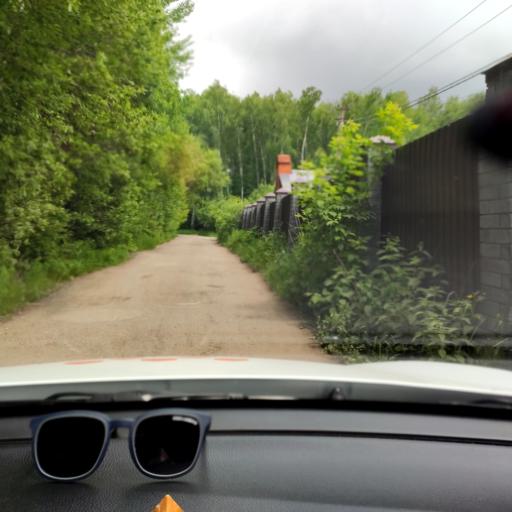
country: RU
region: Tatarstan
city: Vysokaya Gora
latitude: 55.9285
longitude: 49.1622
